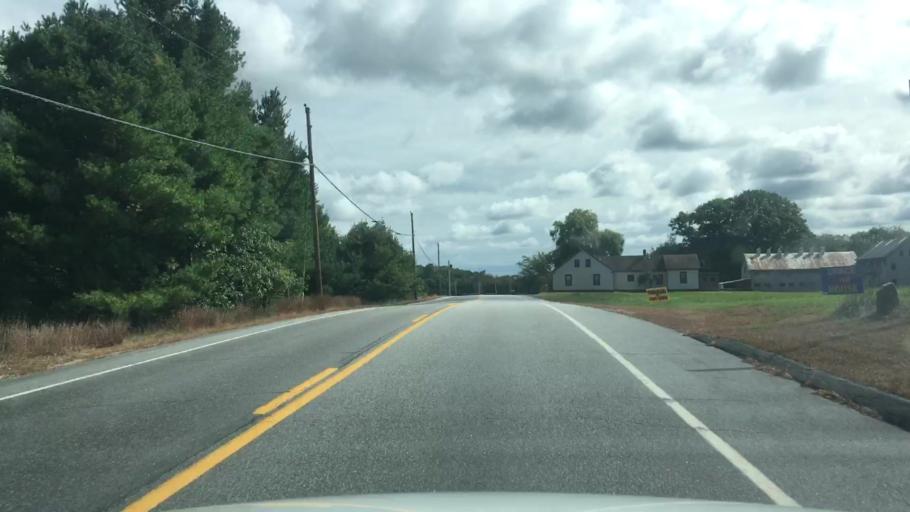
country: US
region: Maine
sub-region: Androscoggin County
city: Lisbon
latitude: 44.0186
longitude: -70.1729
